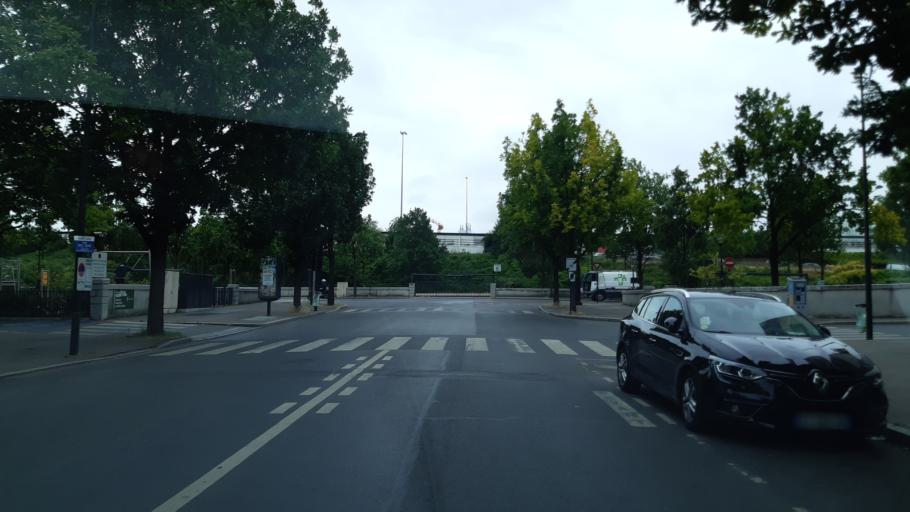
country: FR
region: Ile-de-France
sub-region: Departement de Seine-Saint-Denis
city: Saint-Denis
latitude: 48.9234
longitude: 2.3645
